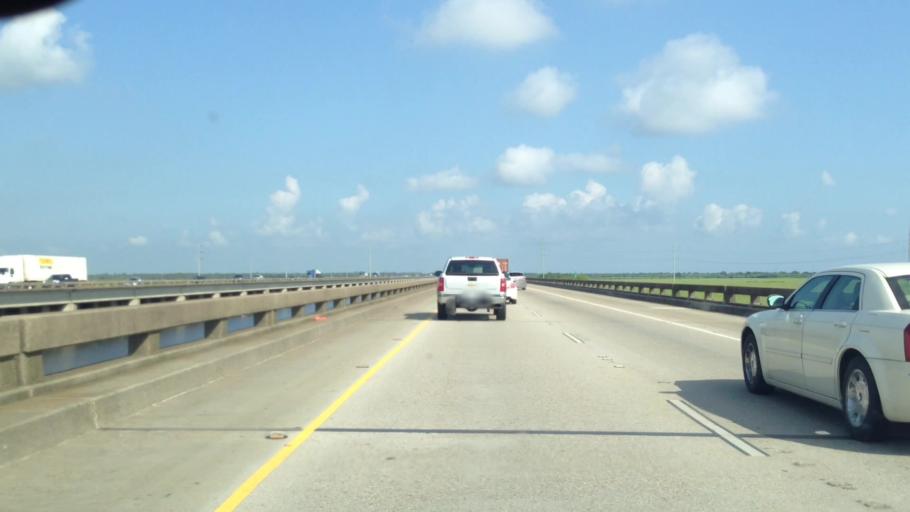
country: US
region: Louisiana
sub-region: Saint Charles Parish
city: New Sarpy
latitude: 30.0340
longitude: -90.3396
